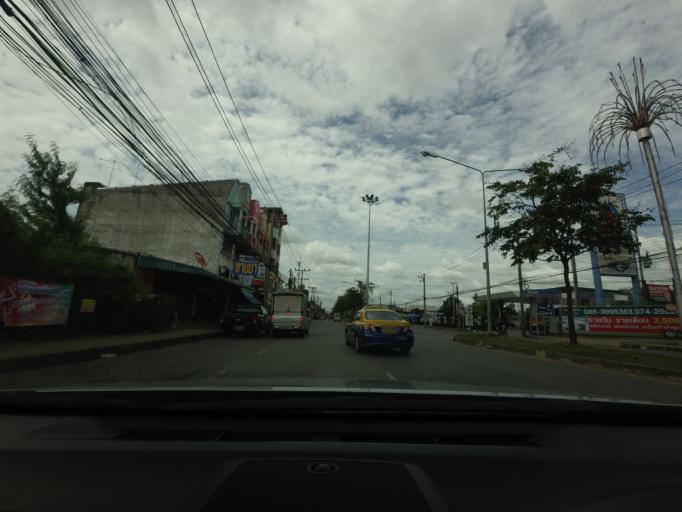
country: TH
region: Songkhla
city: Hat Yai
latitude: 7.0127
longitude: 100.4572
